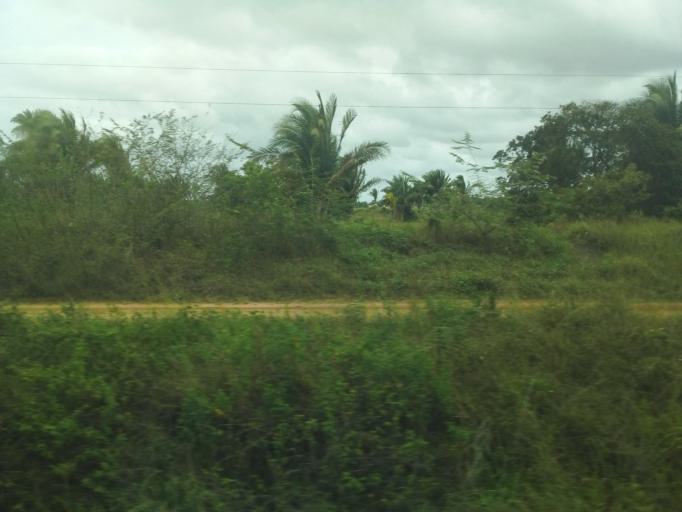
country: BR
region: Maranhao
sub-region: Itapecuru Mirim
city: Itapecuru Mirim
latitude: -3.2170
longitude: -44.4038
